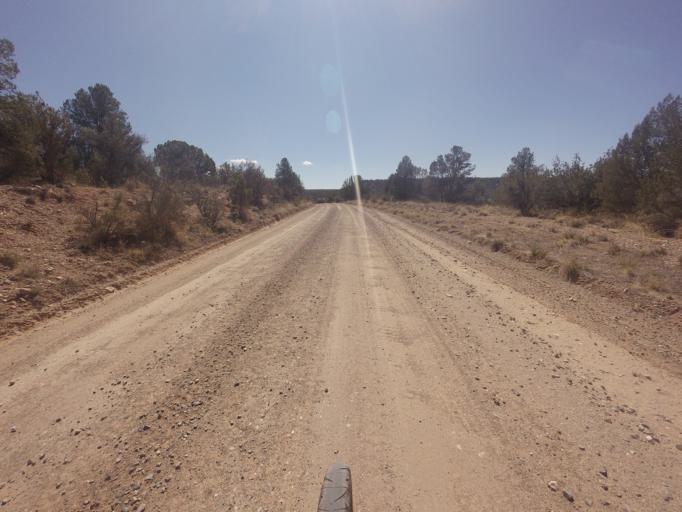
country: US
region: Arizona
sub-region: Yavapai County
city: Lake Montezuma
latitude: 34.6104
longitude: -111.7251
